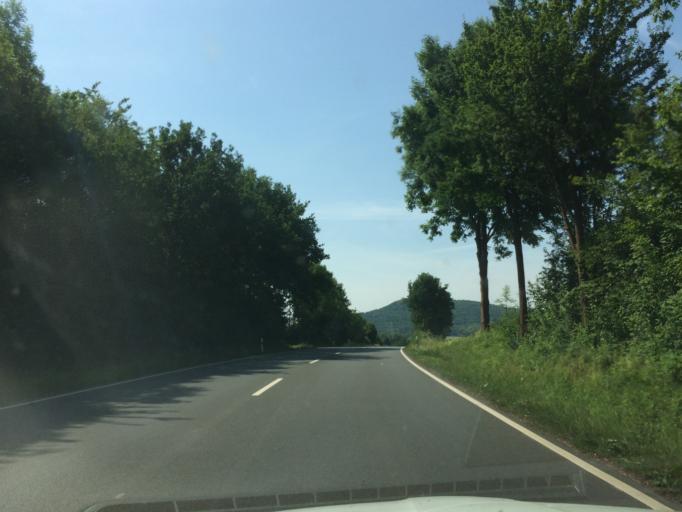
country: DE
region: Hesse
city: Trendelburg
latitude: 51.5448
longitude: 9.4144
